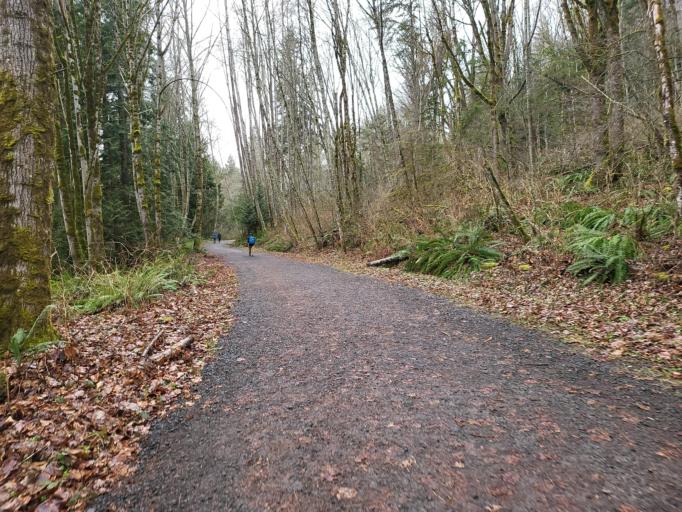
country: US
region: Washington
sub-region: King County
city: Newcastle
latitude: 47.5273
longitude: -122.1215
